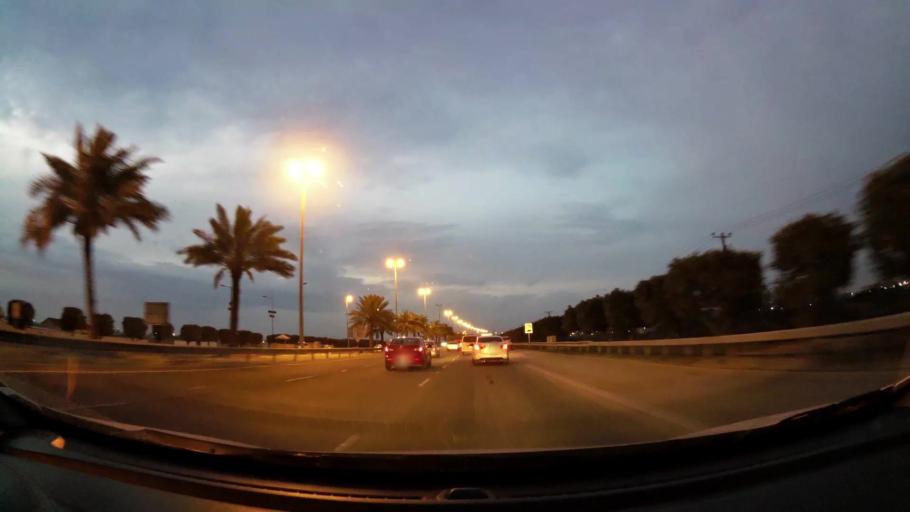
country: BH
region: Northern
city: Madinat `Isa
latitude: 26.1711
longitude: 50.5028
